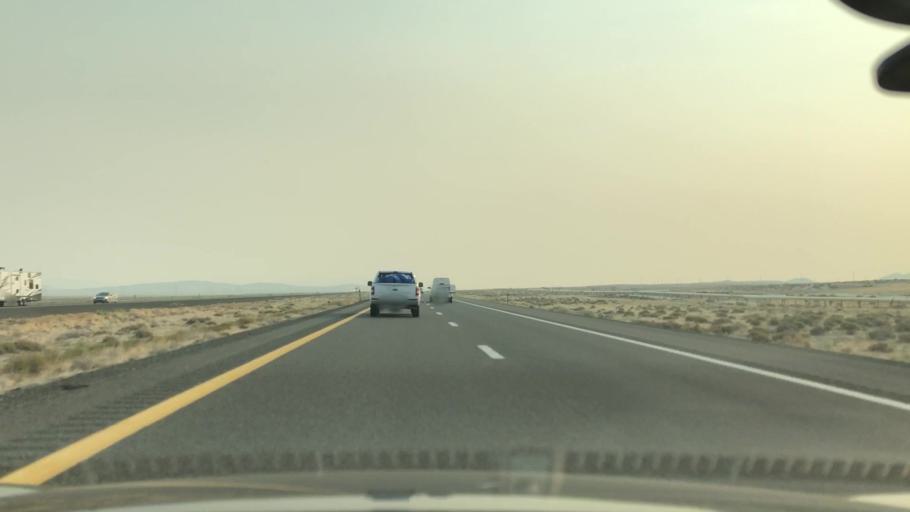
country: US
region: Nevada
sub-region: Lyon County
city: Fernley
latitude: 39.8063
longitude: -119.0071
